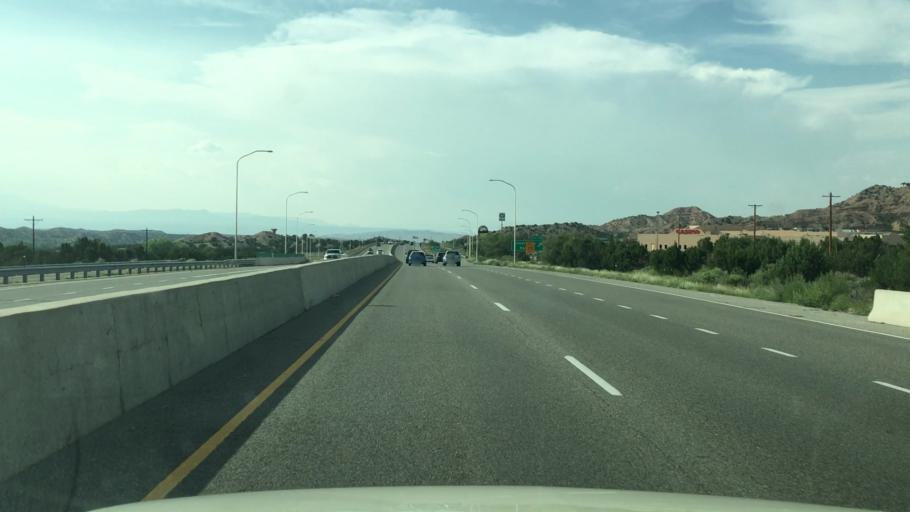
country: US
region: New Mexico
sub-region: Santa Fe County
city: Nambe
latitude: 35.8185
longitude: -105.9729
